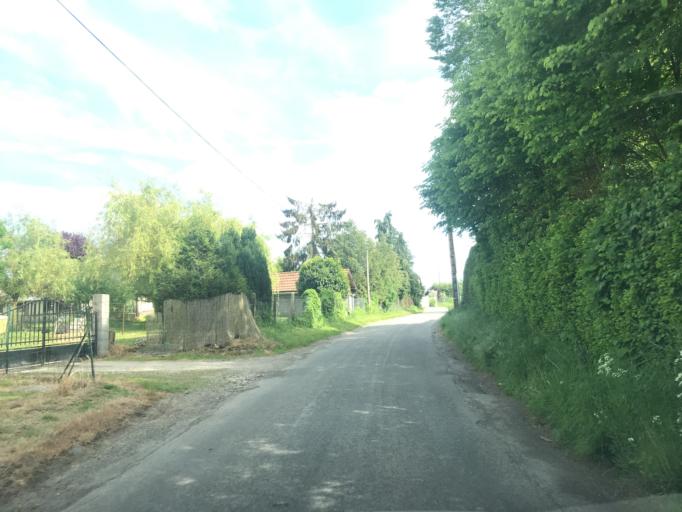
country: FR
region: Haute-Normandie
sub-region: Departement de l'Eure
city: Le Neubourg
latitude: 49.1420
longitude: 0.8393
